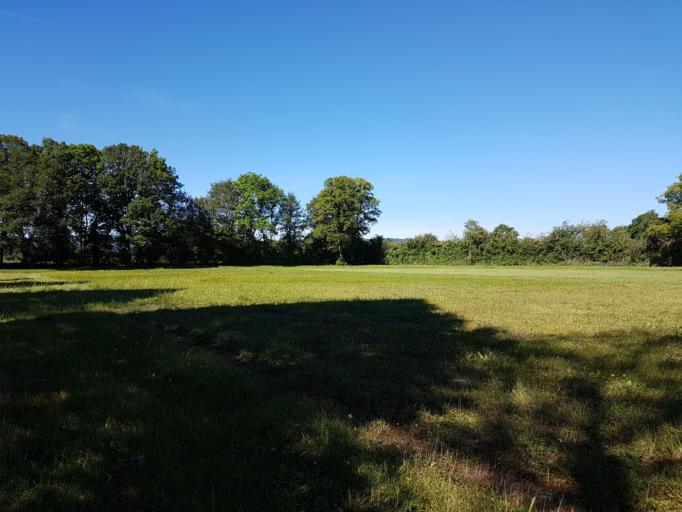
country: FR
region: Bourgogne
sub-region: Departement de Saone-et-Loire
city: Epinac
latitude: 46.9854
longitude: 4.5047
